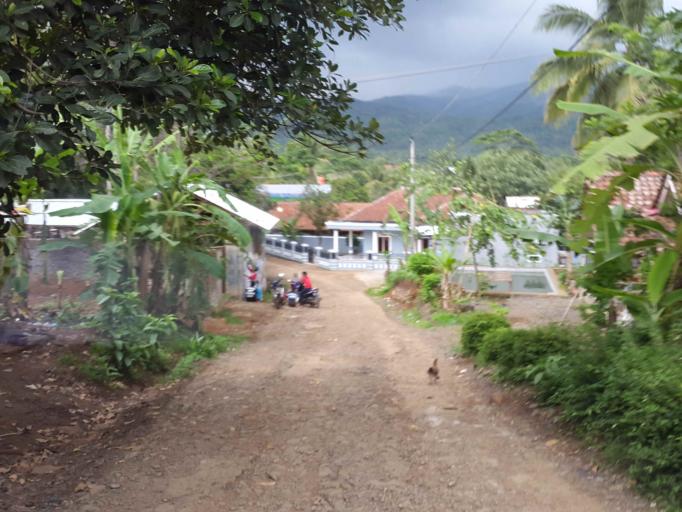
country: ID
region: Central Java
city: Limbangan
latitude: -7.3023
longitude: 108.7077
